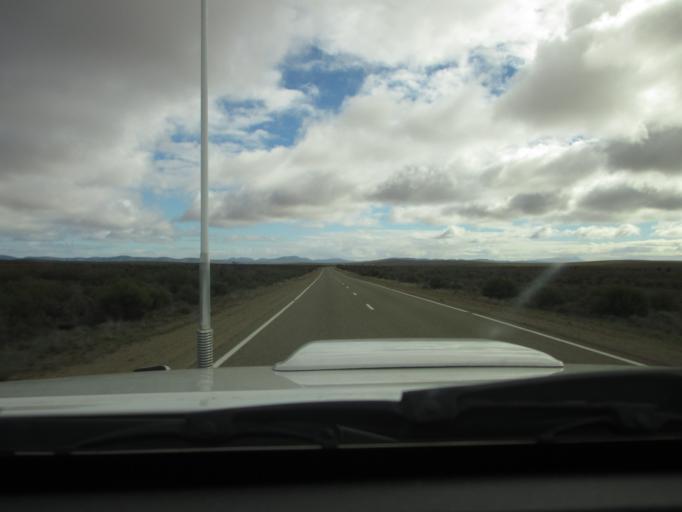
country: AU
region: South Australia
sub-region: Flinders Ranges
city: Quorn
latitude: -32.1254
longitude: 138.5092
